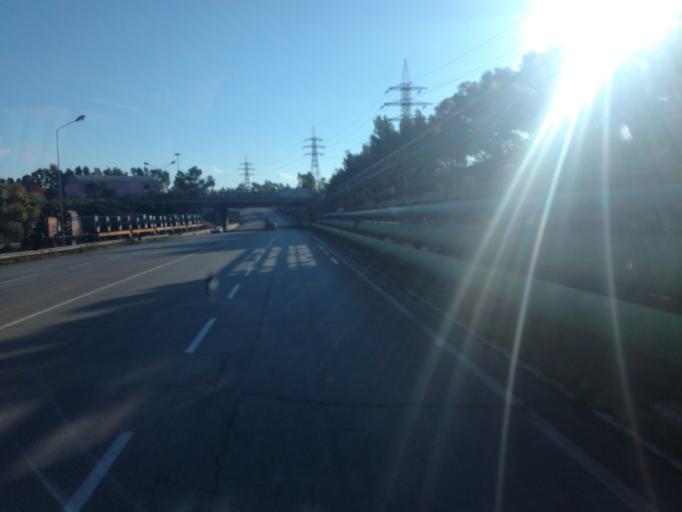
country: IT
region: Apulia
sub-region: Provincia di Taranto
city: Statte
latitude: 40.5138
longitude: 17.1854
